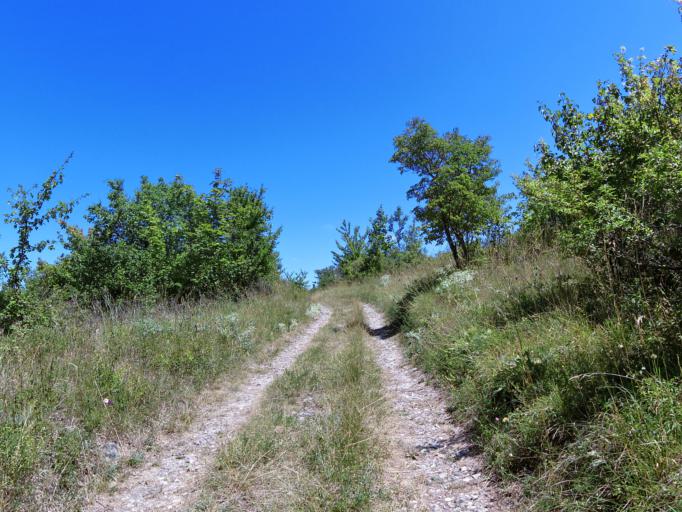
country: DE
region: Bavaria
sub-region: Regierungsbezirk Unterfranken
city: Randersacker
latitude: 49.7592
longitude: 9.9929
